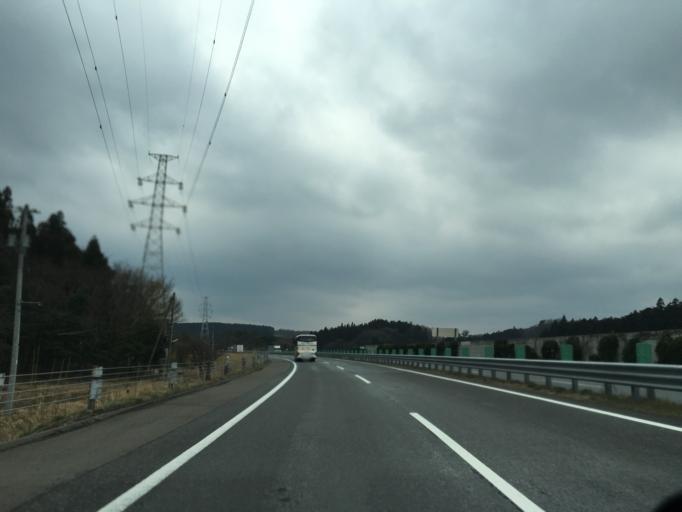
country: JP
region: Tochigi
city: Kuroiso
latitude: 37.1106
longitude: 140.1474
